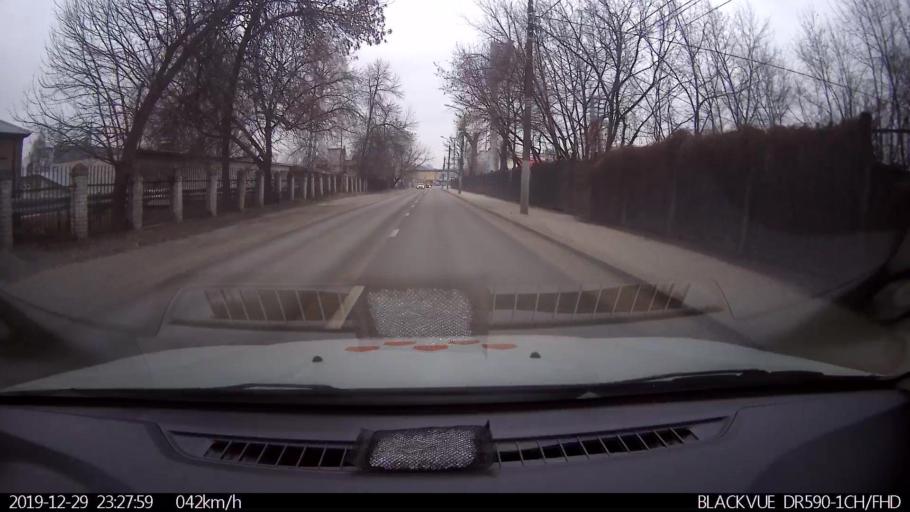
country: RU
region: Nizjnij Novgorod
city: Nizhniy Novgorod
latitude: 56.3074
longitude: 43.9296
